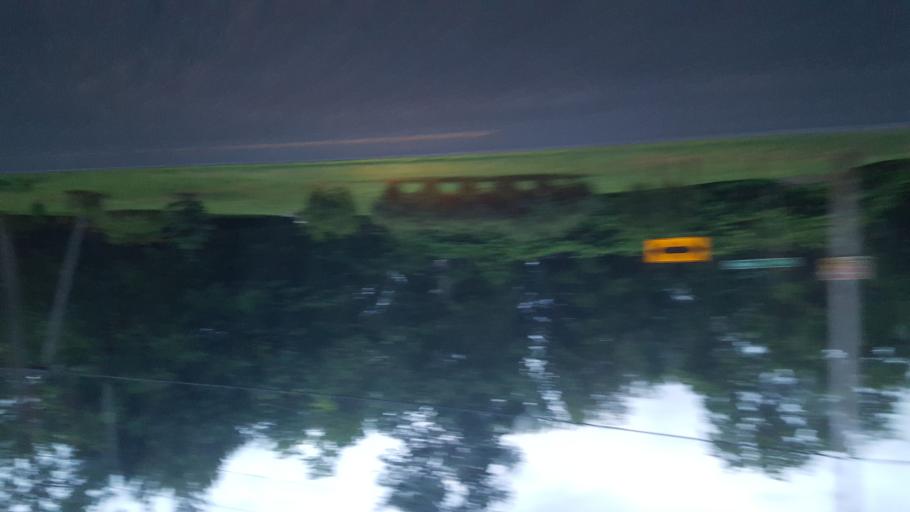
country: US
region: New York
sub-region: Wayne County
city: Clyde
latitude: 43.0256
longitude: -76.9107
